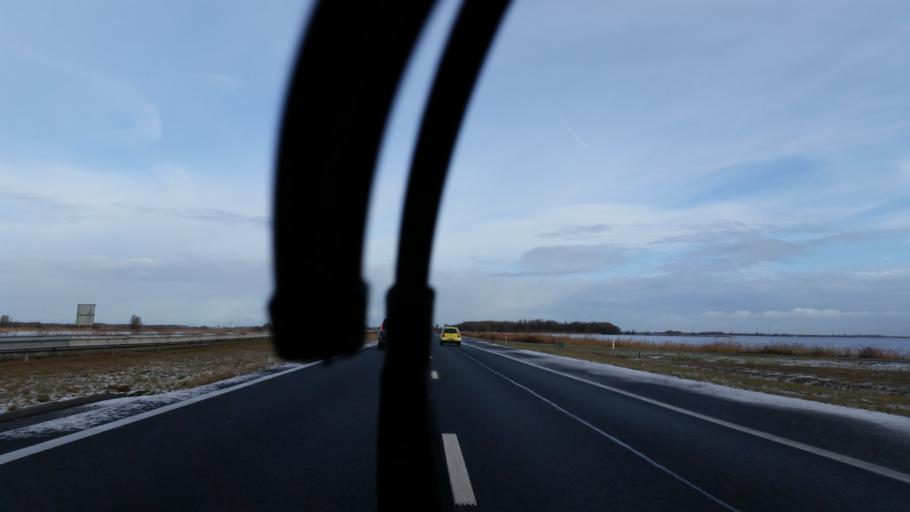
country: NL
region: Friesland
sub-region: Gemeente Skarsterlan
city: Sint Nicolaasga
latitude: 52.8914
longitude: 5.7621
